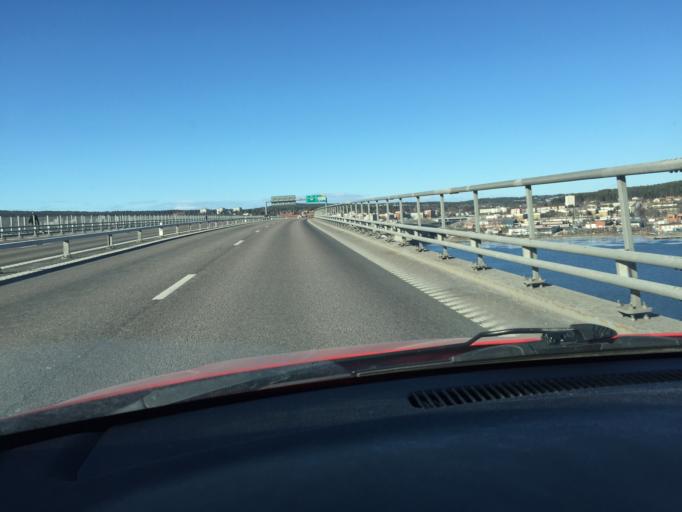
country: SE
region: Vaesternorrland
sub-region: Sundsvalls Kommun
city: Sundsvall
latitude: 62.3869
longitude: 17.3432
